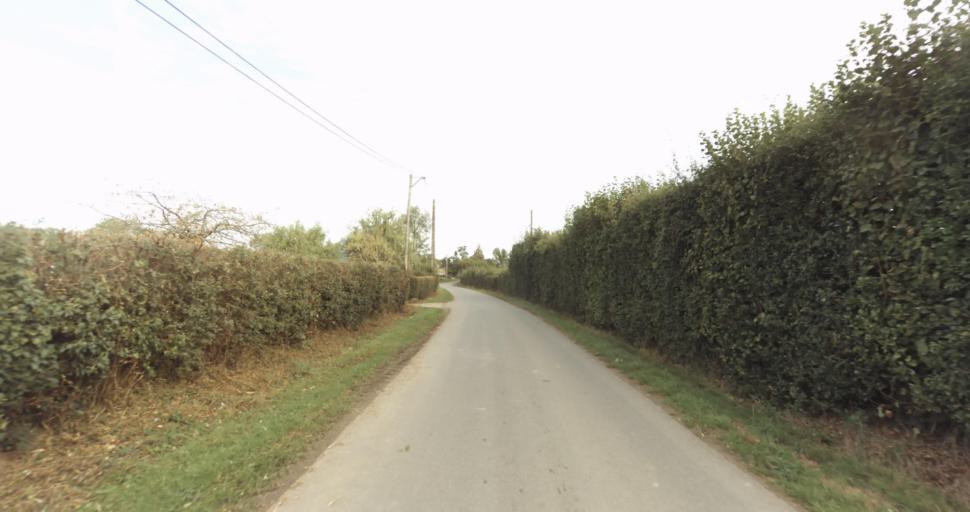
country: FR
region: Lower Normandy
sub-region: Departement de l'Orne
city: Vimoutiers
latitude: 48.8906
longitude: 0.2360
